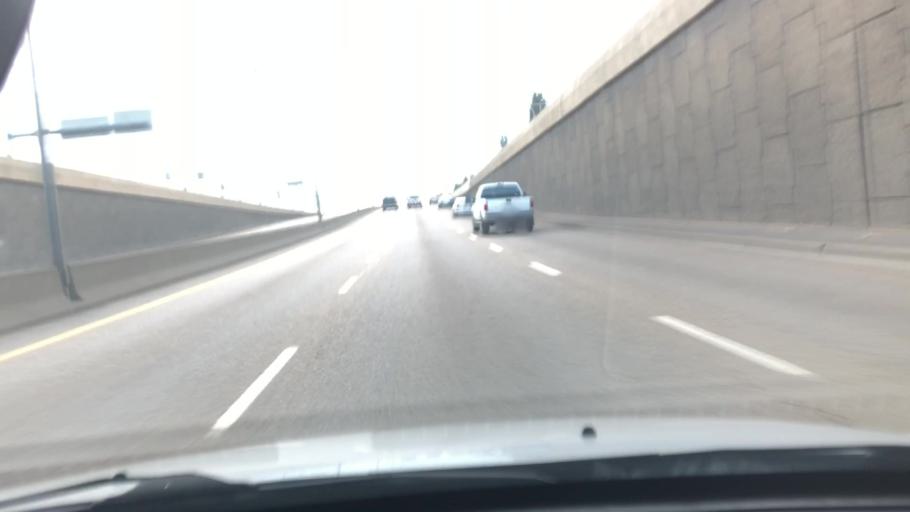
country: CA
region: Alberta
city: Edmonton
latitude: 53.5813
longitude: -113.4916
